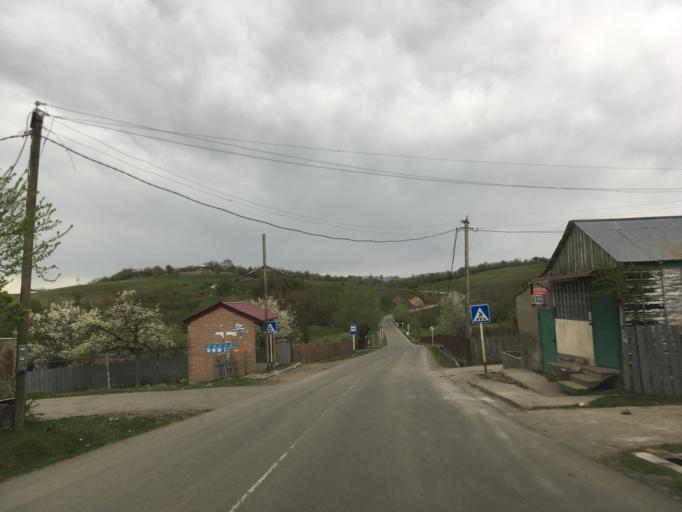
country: GE
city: Surami
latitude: 42.2097
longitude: 43.3878
